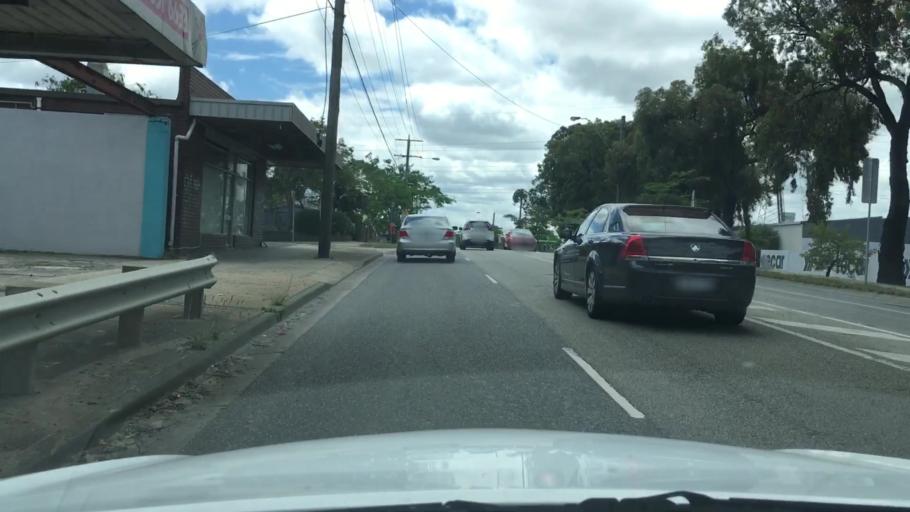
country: AU
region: Victoria
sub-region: Kingston
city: Clayton South
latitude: -37.9404
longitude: 145.1167
